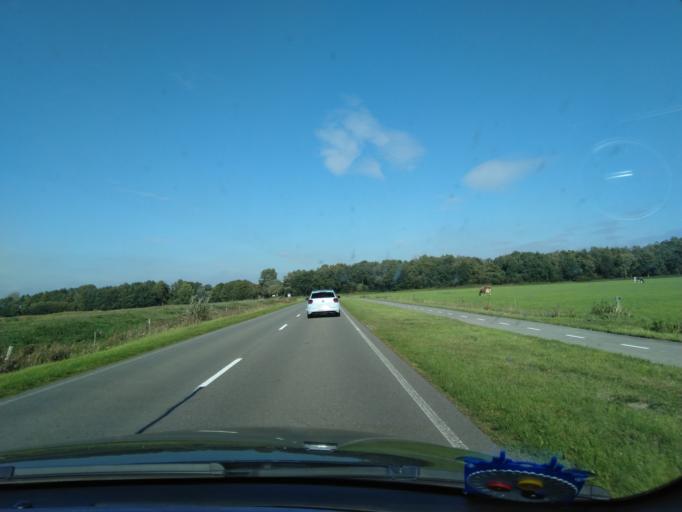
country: NL
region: Drenthe
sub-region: Gemeente Aa en Hunze
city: Anloo
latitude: 53.0718
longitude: 6.7616
